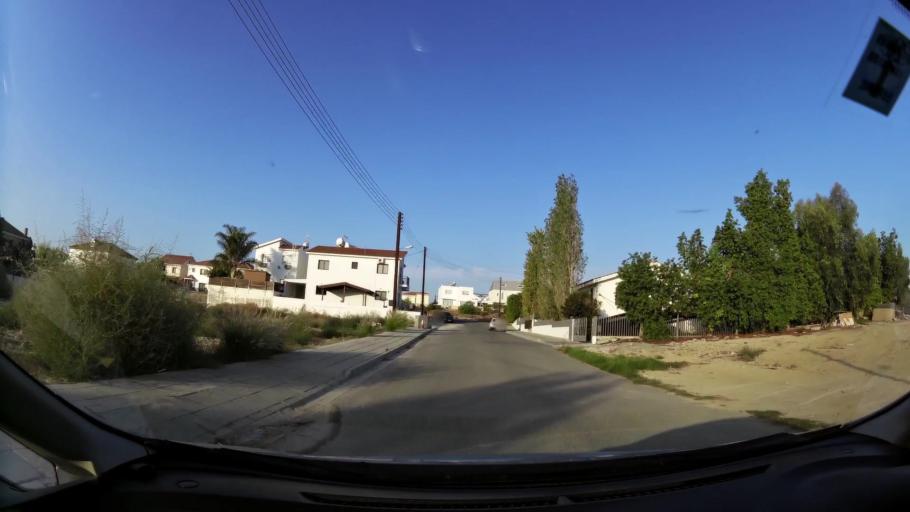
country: CY
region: Larnaka
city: Aradippou
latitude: 34.9289
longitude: 33.5898
